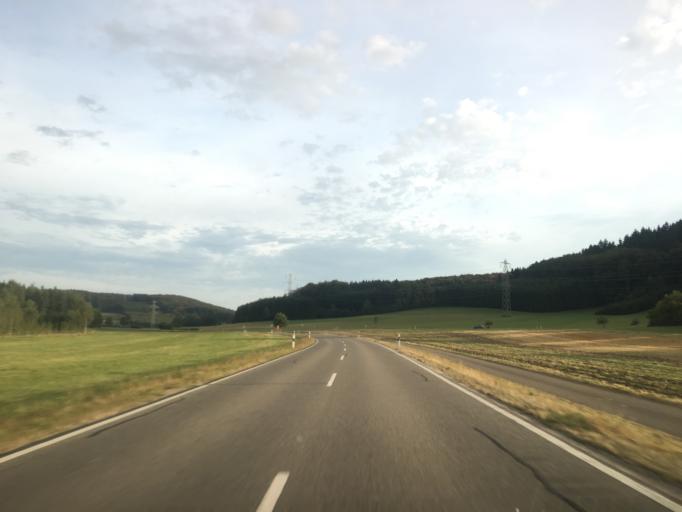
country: DE
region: Baden-Wuerttemberg
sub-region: Tuebingen Region
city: Sankt Johann
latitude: 48.4409
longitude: 9.3489
